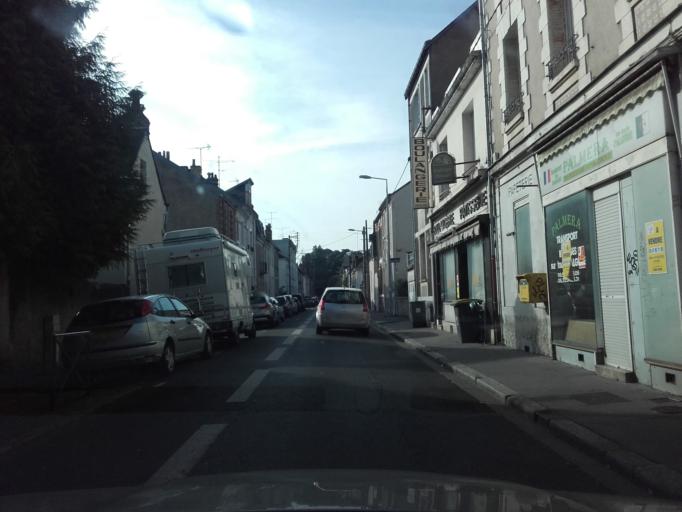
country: FR
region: Centre
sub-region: Departement d'Indre-et-Loire
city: Tours
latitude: 47.3847
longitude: 0.7038
